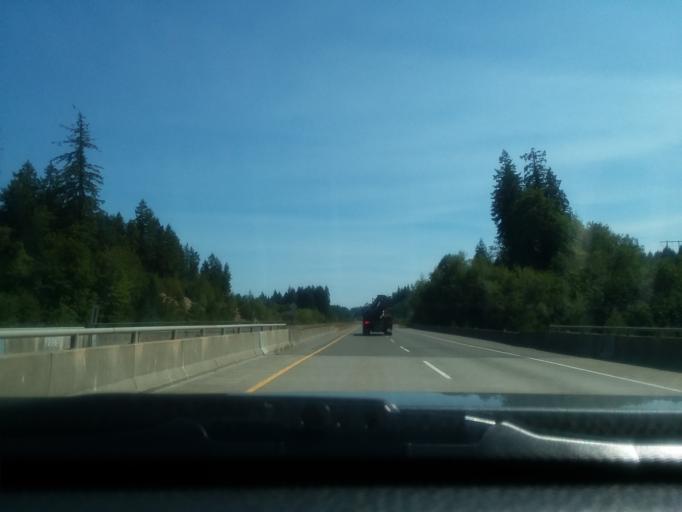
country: CA
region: British Columbia
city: Port Alberni
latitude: 49.4408
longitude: -124.7582
